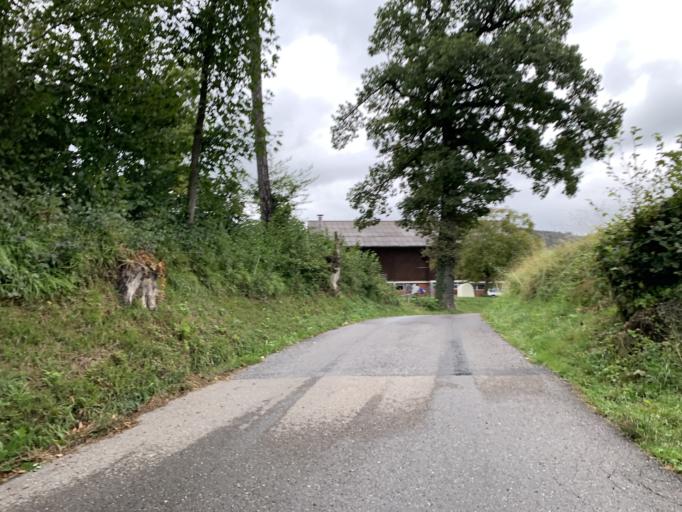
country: CH
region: Zurich
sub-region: Bezirk Hinwil
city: Hadlikon
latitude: 47.3047
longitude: 8.8600
